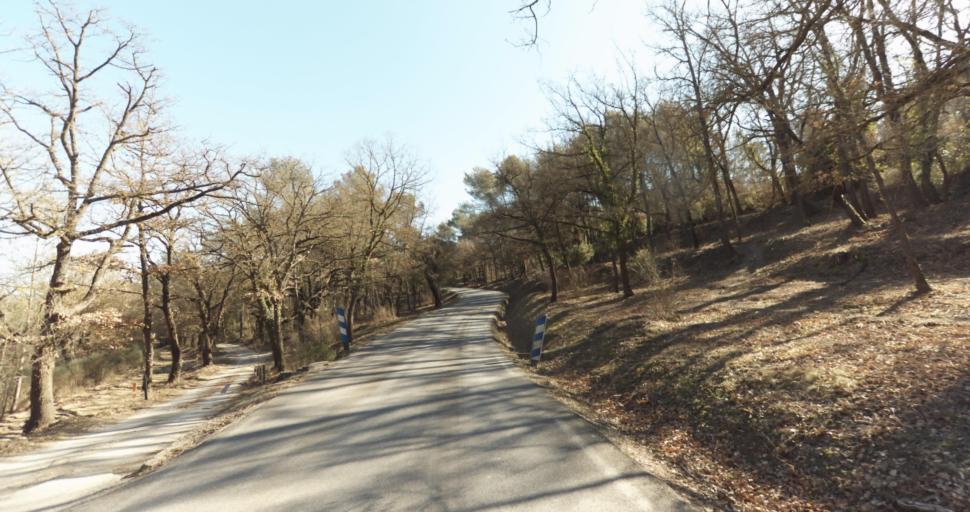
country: FR
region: Provence-Alpes-Cote d'Azur
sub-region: Departement des Bouches-du-Rhone
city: Peypin
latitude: 43.3944
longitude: 5.5672
